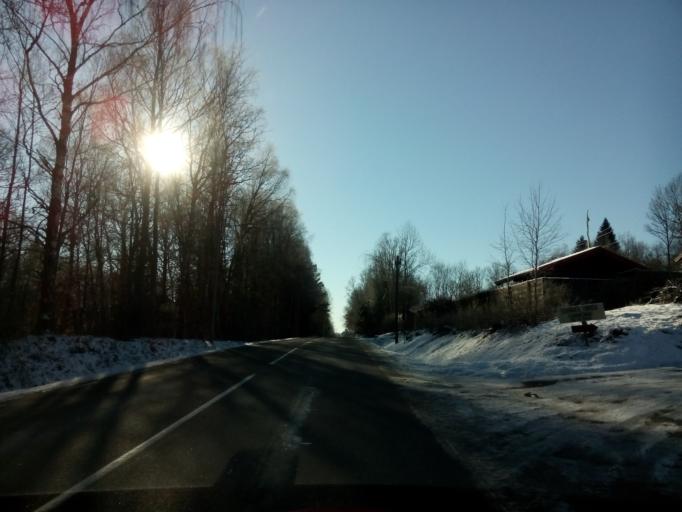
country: SE
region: Vaestra Goetaland
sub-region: Herrljunga Kommun
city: Herrljunga
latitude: 57.9055
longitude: 13.0194
